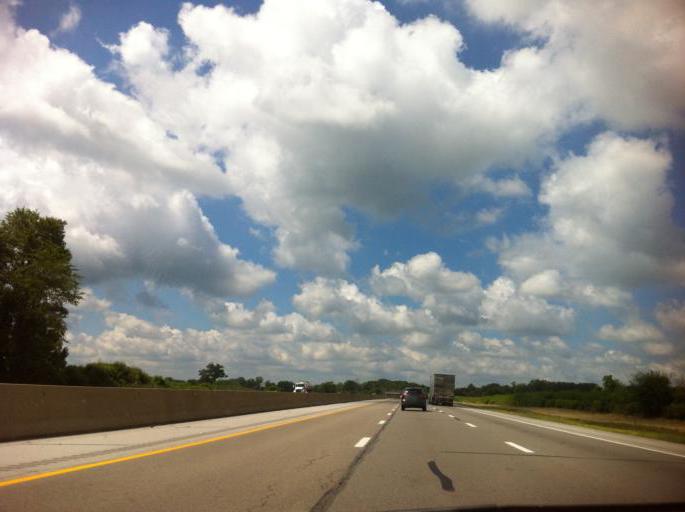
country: US
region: Ohio
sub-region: Erie County
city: Milan
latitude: 41.3236
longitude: -82.5716
